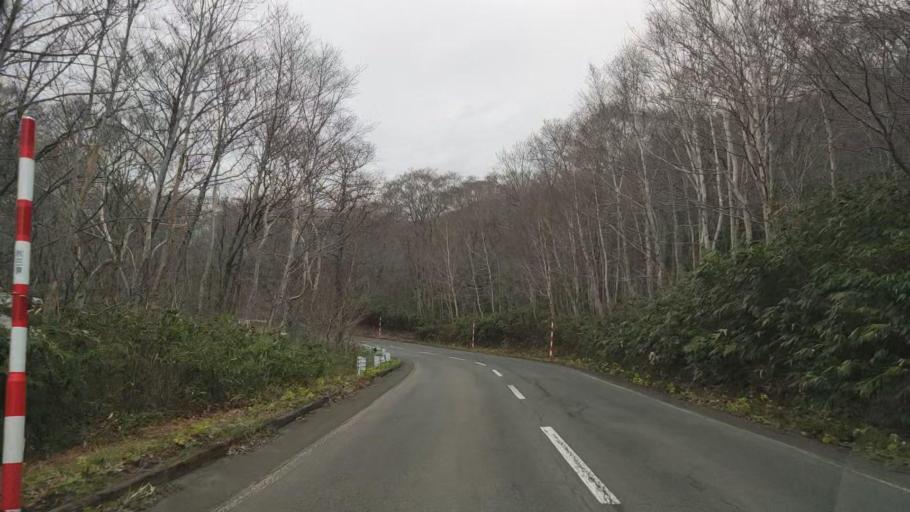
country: JP
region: Akita
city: Hanawa
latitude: 40.4212
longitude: 140.8365
